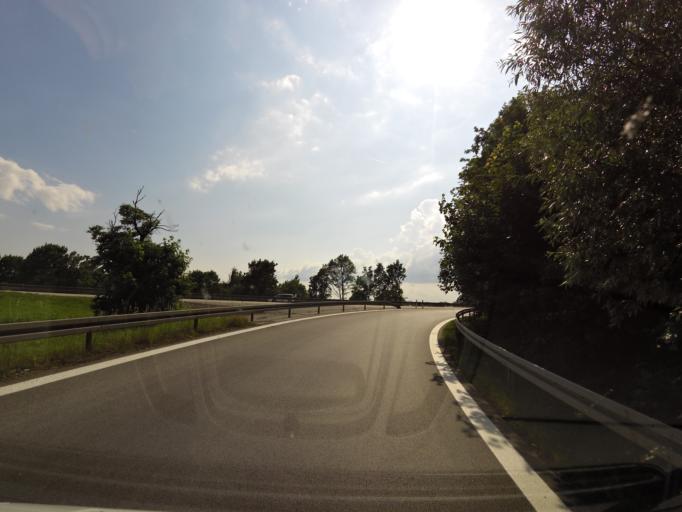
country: DE
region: Bavaria
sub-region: Lower Bavaria
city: Hengersberg
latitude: 48.7706
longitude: 13.0429
